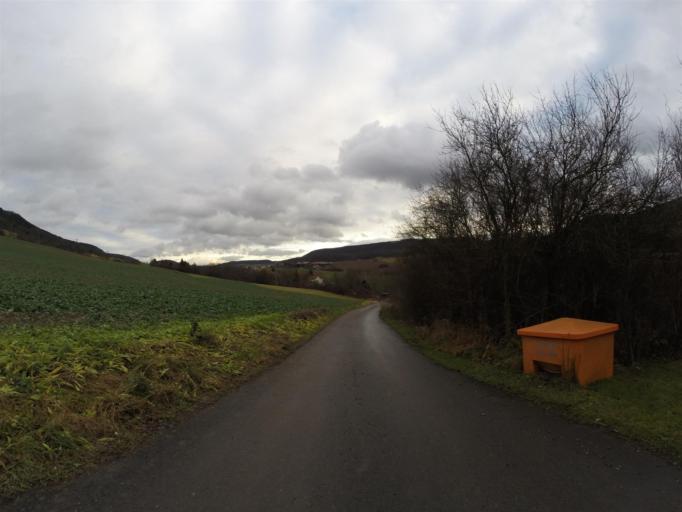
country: DE
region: Thuringia
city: Golmsdorf
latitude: 50.9341
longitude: 11.6376
